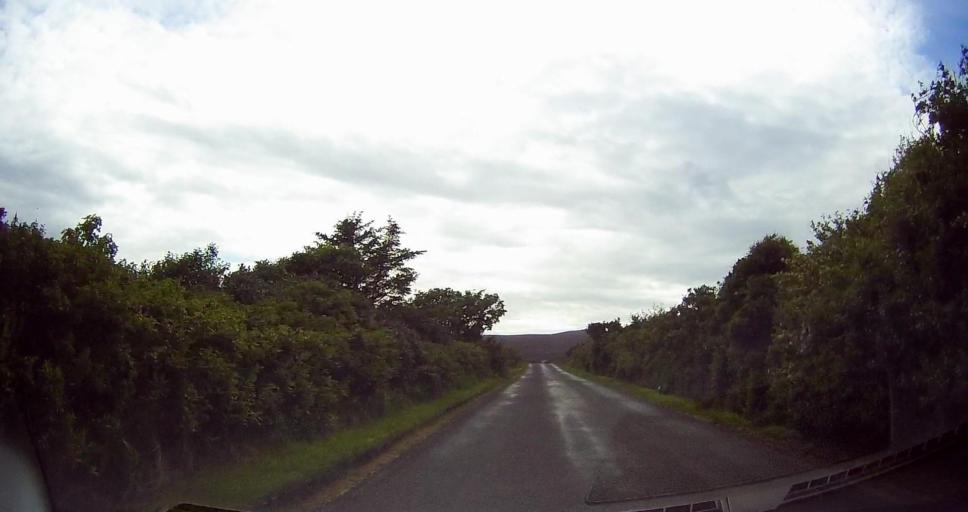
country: GB
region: Scotland
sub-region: Orkney Islands
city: Stromness
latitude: 58.8032
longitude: -3.2311
